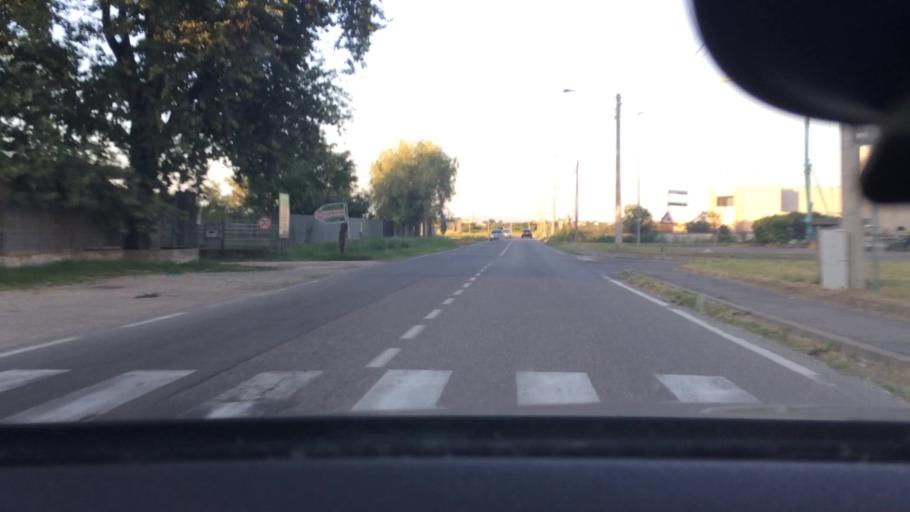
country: IT
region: Lombardy
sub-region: Provincia di Varese
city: Cislago
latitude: 45.6346
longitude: 8.9751
